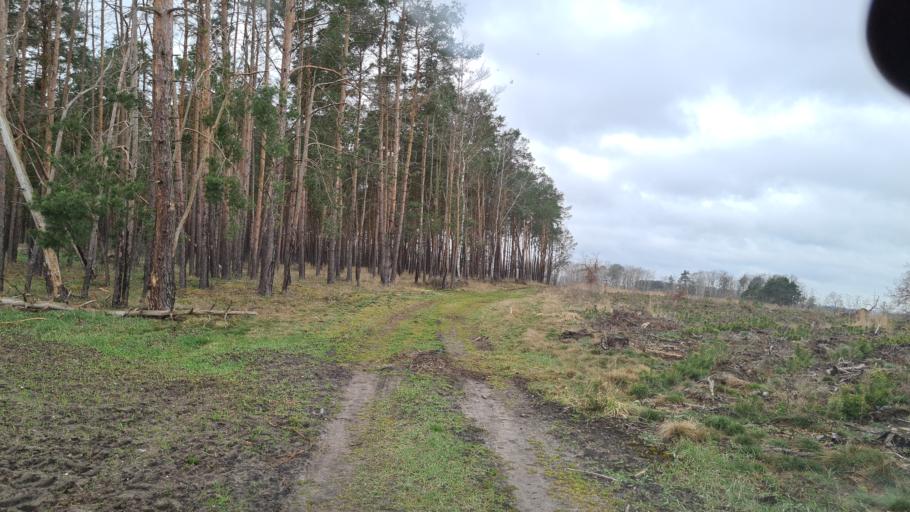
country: DE
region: Brandenburg
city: Schonewalde
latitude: 51.6468
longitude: 13.6188
